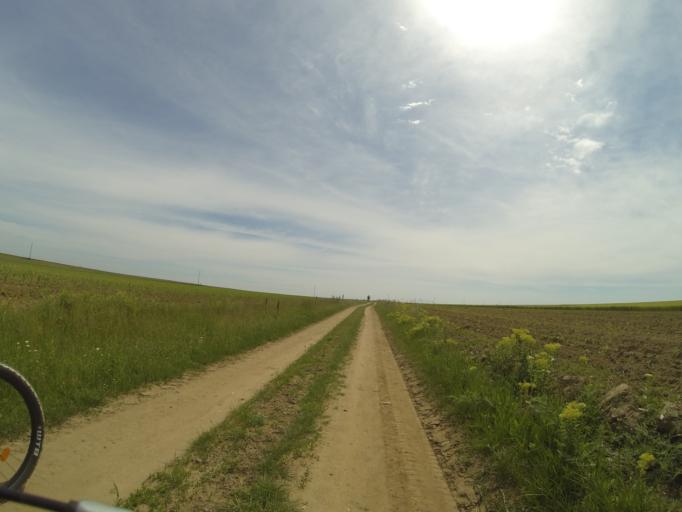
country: RO
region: Dolj
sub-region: Comuna Ghindeni
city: Ghindeni
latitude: 44.2074
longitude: 23.9404
